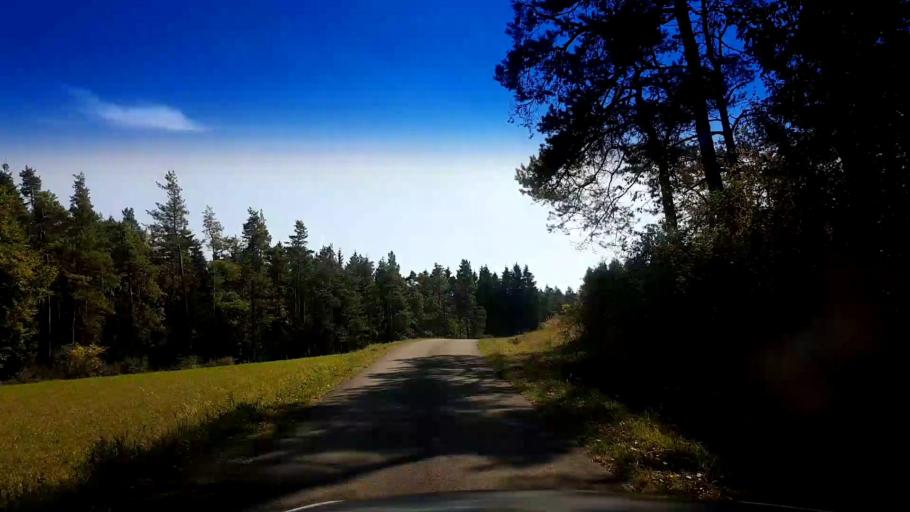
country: DE
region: Bavaria
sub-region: Upper Franconia
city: Poxdorf
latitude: 49.8798
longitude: 11.0897
